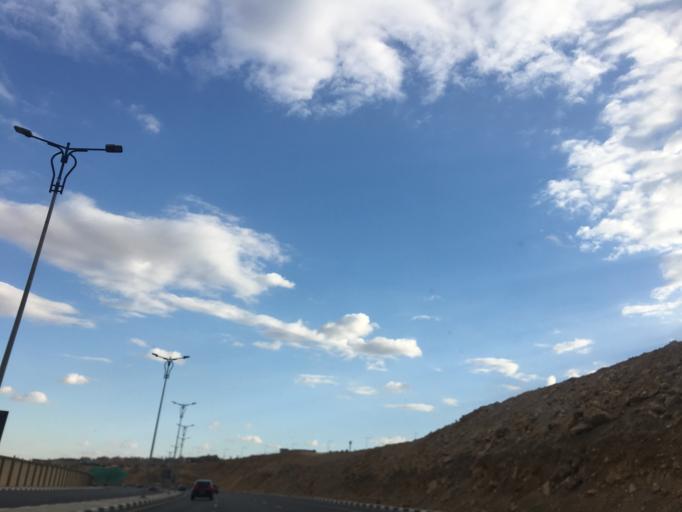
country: EG
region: Muhafazat al Qahirah
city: Cairo
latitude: 30.0303
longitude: 31.3094
